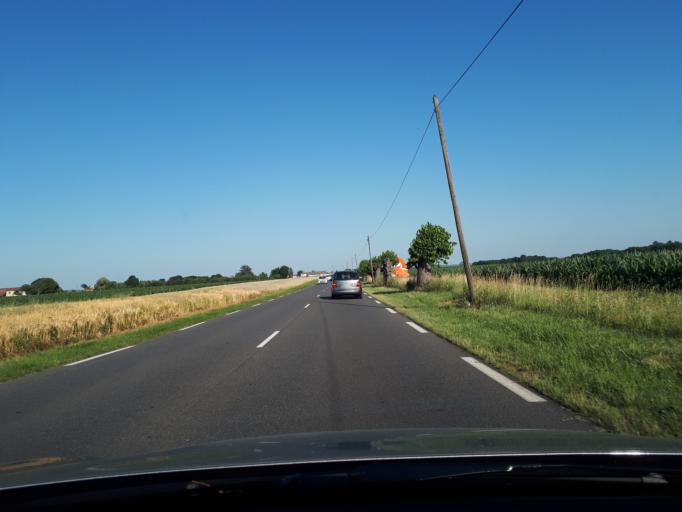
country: FR
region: Rhone-Alpes
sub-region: Departement du Rhone
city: Saint-Bonnet-de-Mure
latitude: 45.7228
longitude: 5.0433
